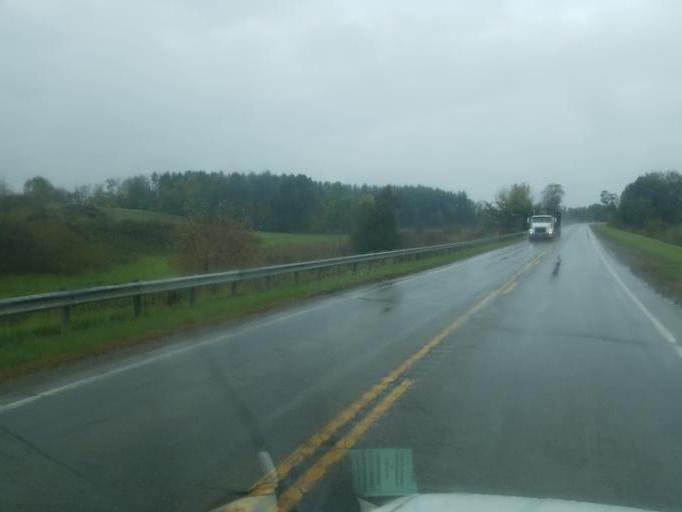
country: US
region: Ohio
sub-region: Holmes County
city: Millersburg
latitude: 40.6223
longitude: -81.9219
